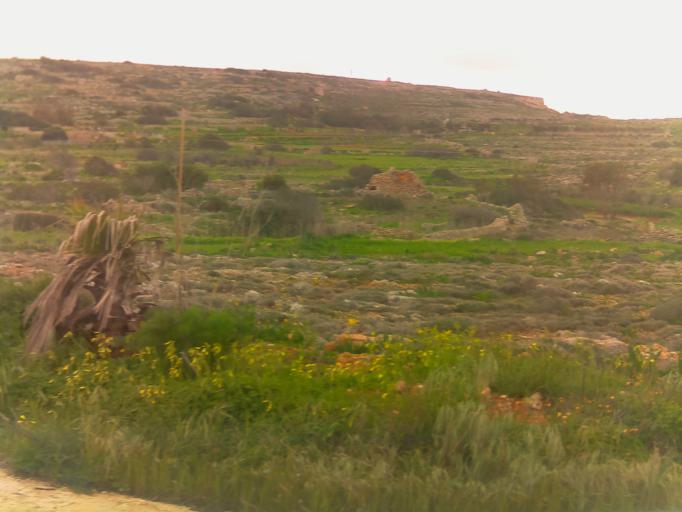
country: MT
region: Il-Mellieha
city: Mellieha
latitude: 35.9797
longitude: 14.3350
